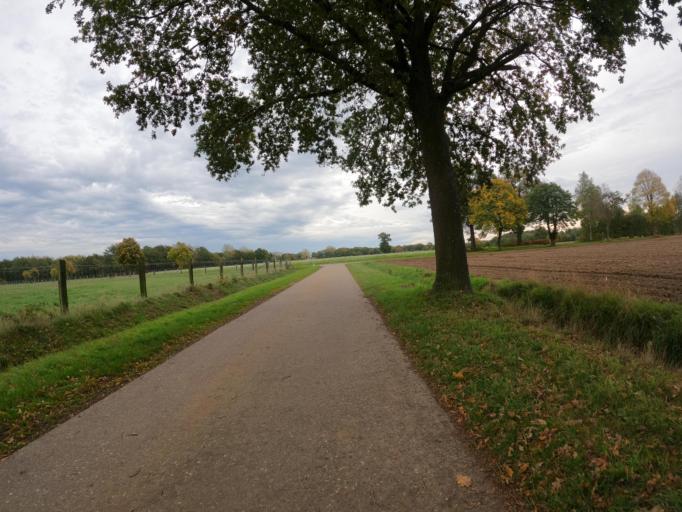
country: BE
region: Flanders
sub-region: Provincie Antwerpen
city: Hulshout
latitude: 51.1057
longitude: 4.8175
